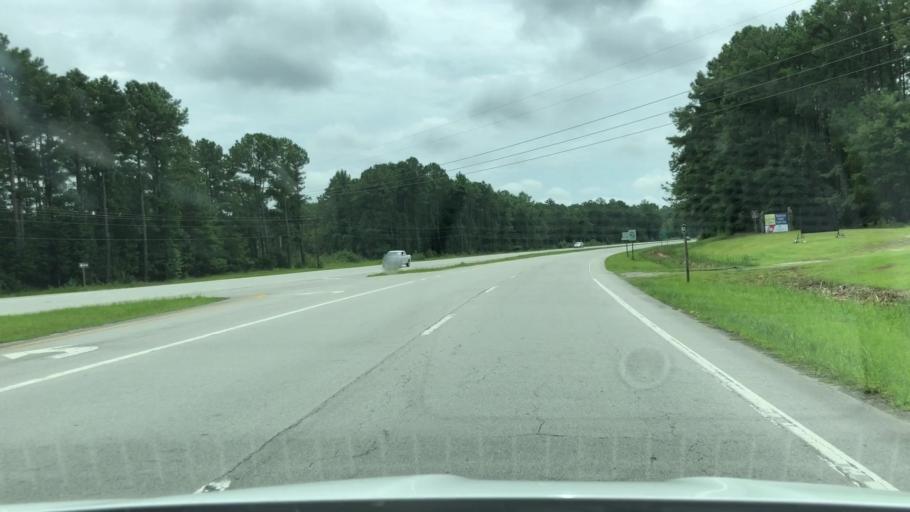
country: US
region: North Carolina
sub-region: Craven County
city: Havelock
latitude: 34.8445
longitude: -76.8831
